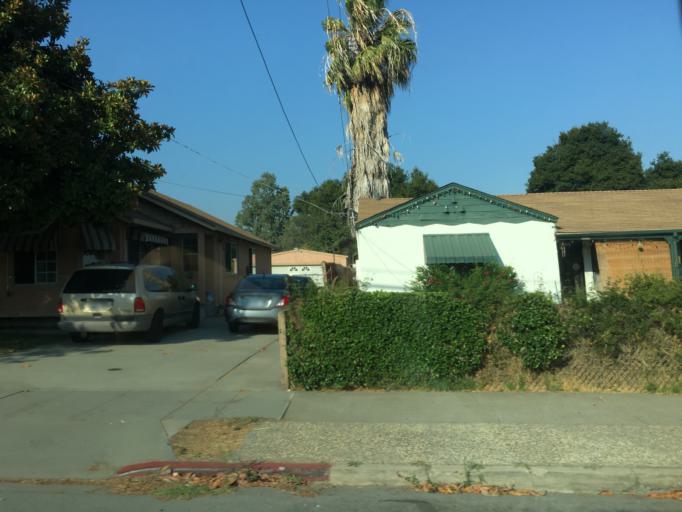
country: US
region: California
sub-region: Santa Clara County
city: Alum Rock
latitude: 37.3680
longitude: -121.8299
